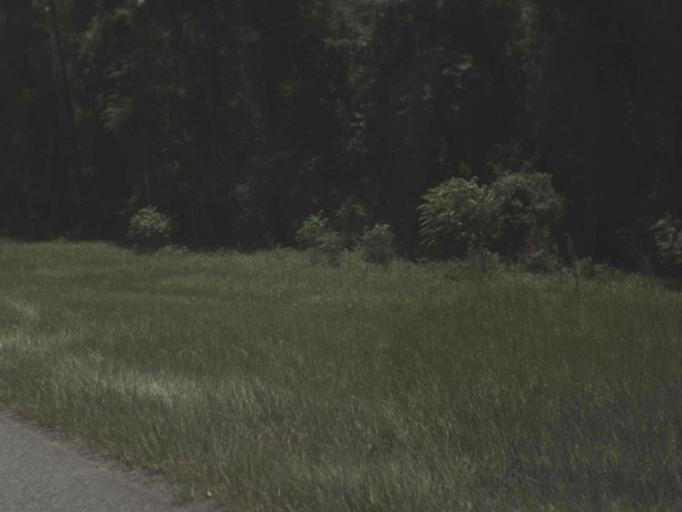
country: US
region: Florida
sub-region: Suwannee County
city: Live Oak
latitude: 30.3909
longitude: -83.1839
